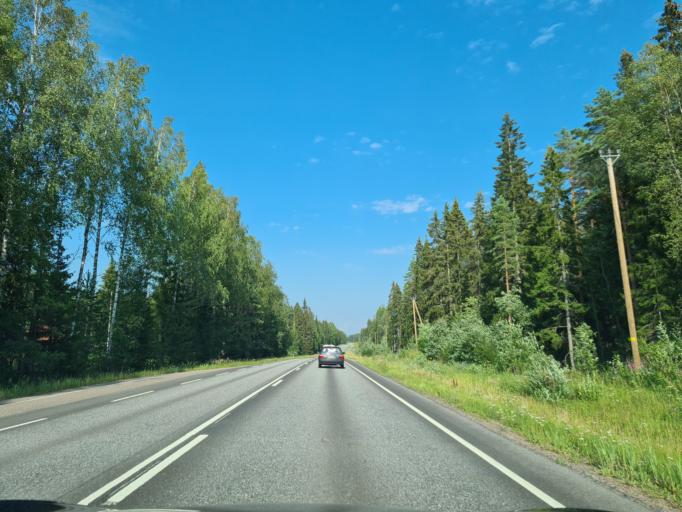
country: FI
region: Satakunta
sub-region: Pori
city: Laengelmaeki
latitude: 61.7679
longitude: 22.1589
